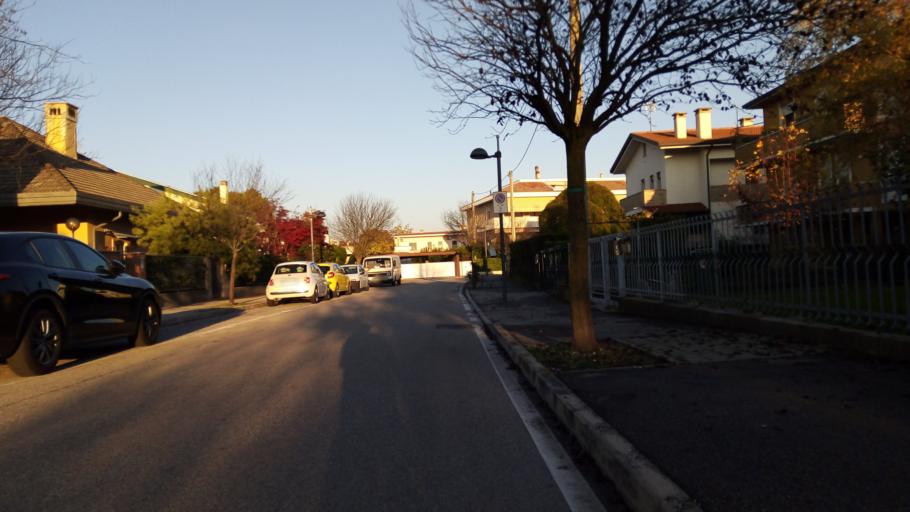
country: IT
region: Veneto
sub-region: Provincia di Padova
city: Abano Terme
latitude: 45.3689
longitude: 11.7933
